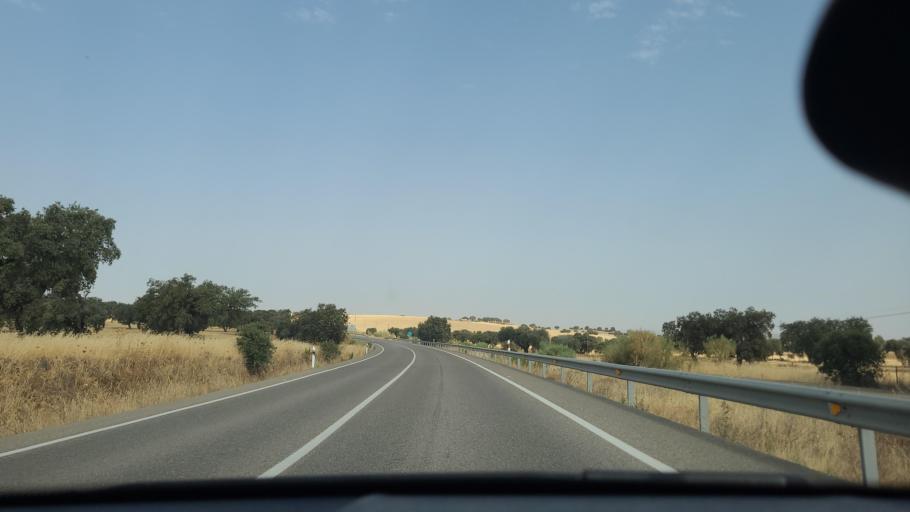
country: ES
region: Extremadura
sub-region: Provincia de Badajoz
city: Granja de Torrehermosa
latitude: 38.2854
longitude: -5.5210
